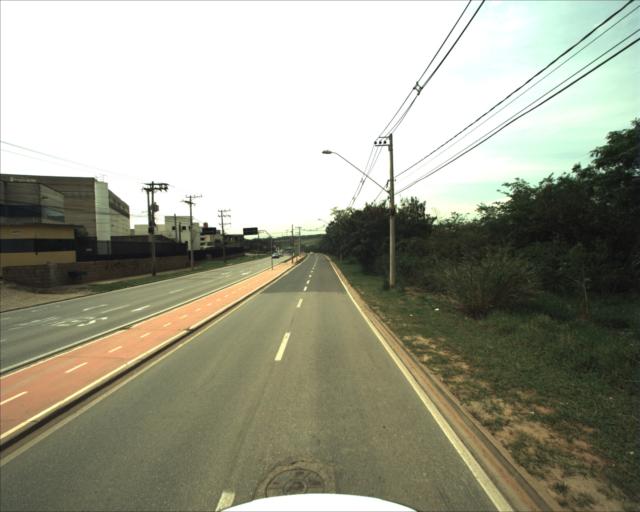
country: BR
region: Sao Paulo
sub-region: Sorocaba
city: Sorocaba
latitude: -23.4332
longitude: -47.4362
